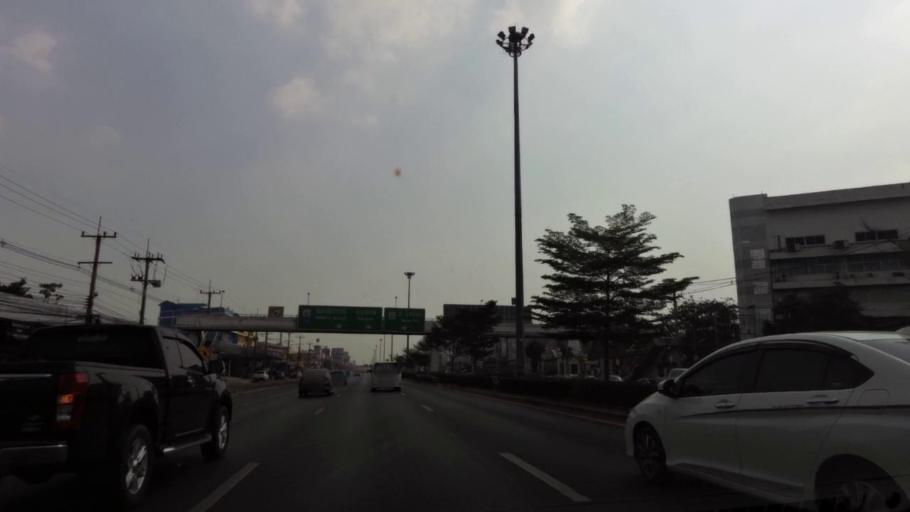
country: TH
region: Phra Nakhon Si Ayutthaya
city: Phra Nakhon Si Ayutthaya
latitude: 14.3514
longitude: 100.6020
